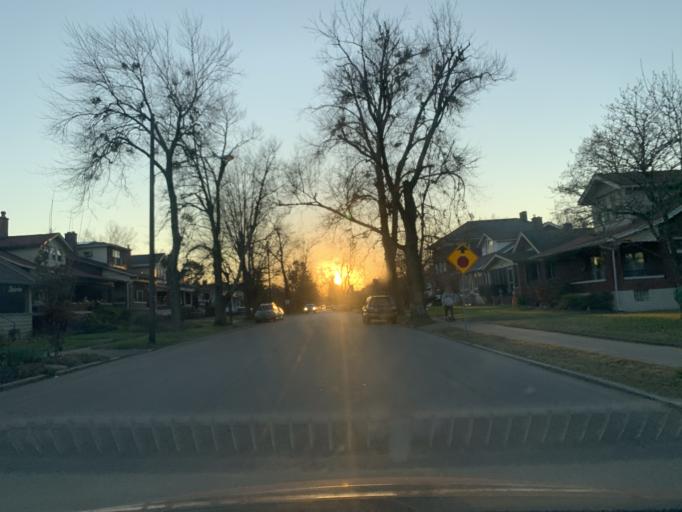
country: US
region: Kentucky
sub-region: Jefferson County
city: West Buechel
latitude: 38.2266
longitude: -85.6864
